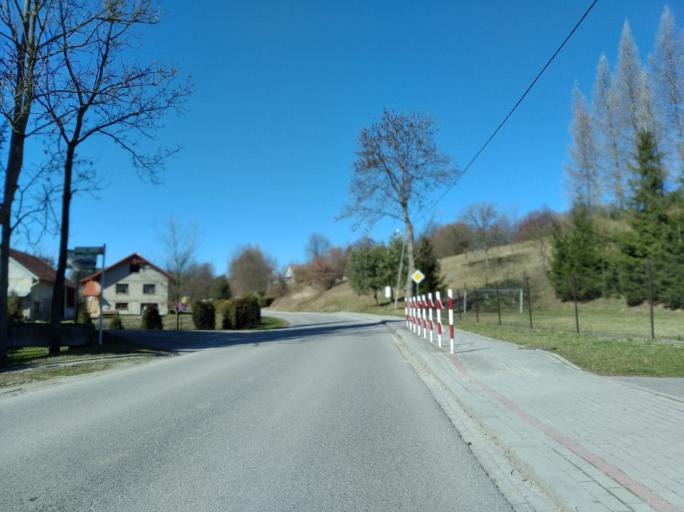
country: PL
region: Subcarpathian Voivodeship
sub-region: Powiat strzyzowski
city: Wisniowa
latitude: 49.8879
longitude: 21.6691
